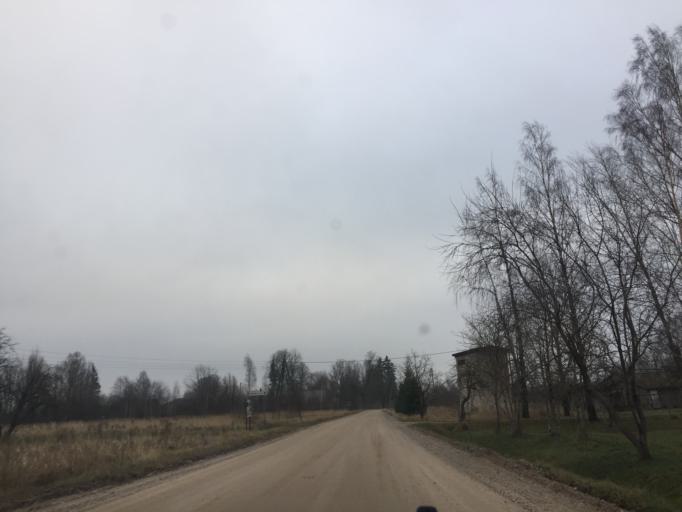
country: LV
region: Limbazu Rajons
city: Limbazi
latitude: 57.5965
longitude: 24.5145
